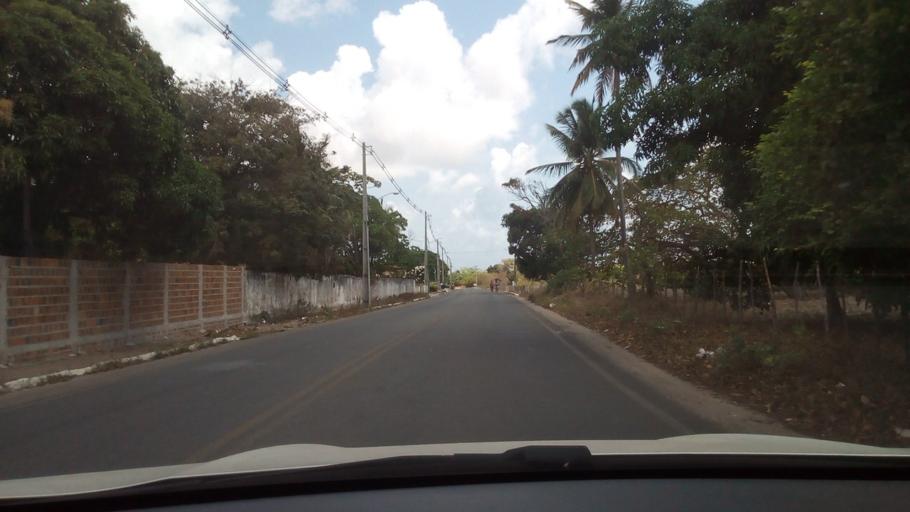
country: BR
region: Paraiba
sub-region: Conde
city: Conde
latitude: -7.2080
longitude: -34.8277
